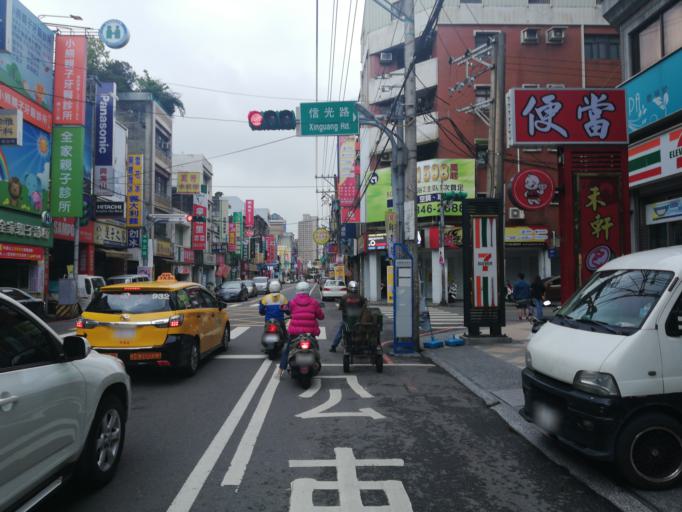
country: TW
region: Taiwan
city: Taoyuan City
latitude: 25.0046
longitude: 121.3048
